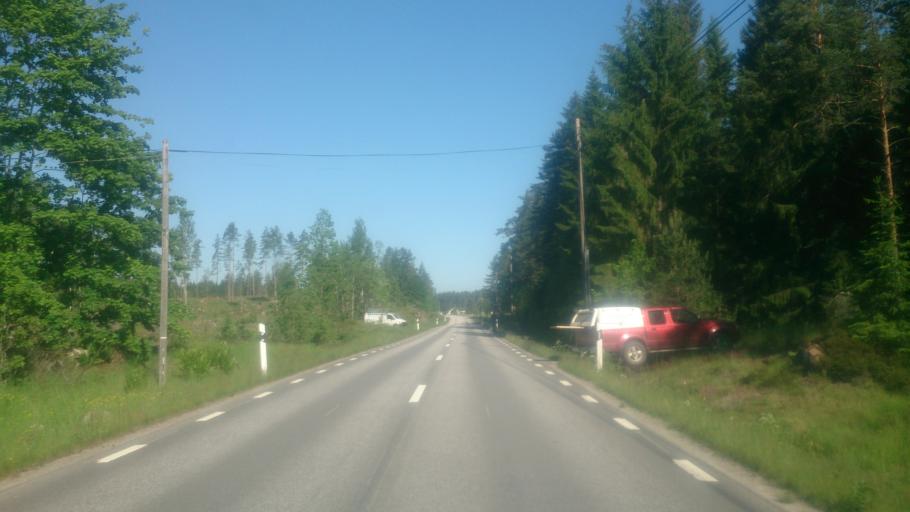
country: SE
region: OEstergoetland
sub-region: Atvidabergs Kommun
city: Atvidaberg
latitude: 58.1064
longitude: 16.1106
